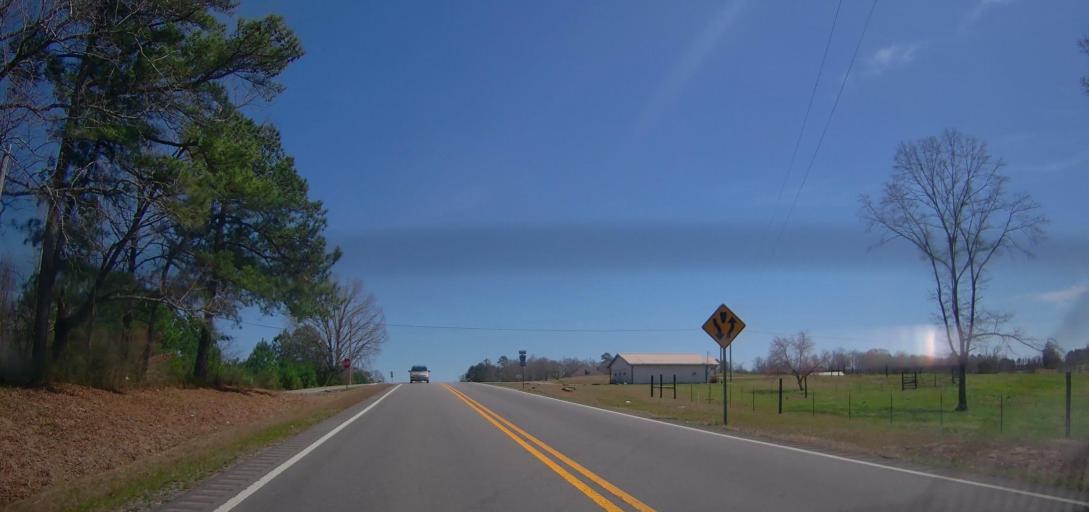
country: US
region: Alabama
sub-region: Blount County
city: Blountsville
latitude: 34.1715
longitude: -86.5268
